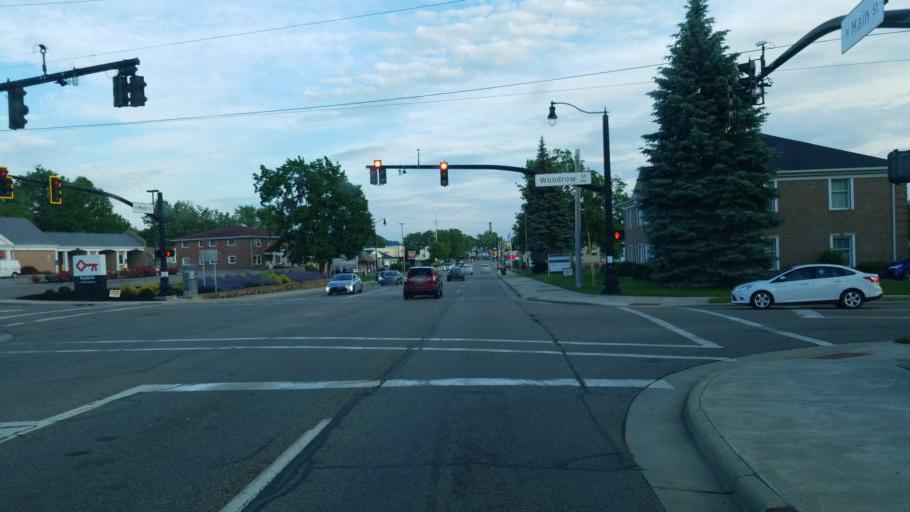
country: US
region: Ohio
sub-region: Stark County
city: North Canton
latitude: 40.8860
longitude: -81.4045
